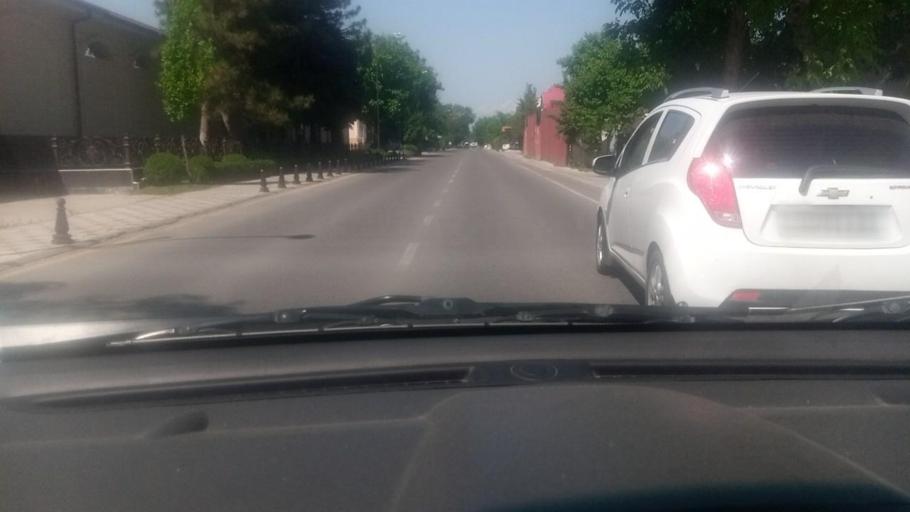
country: UZ
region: Toshkent
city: Salor
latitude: 41.3307
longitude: 69.3563
